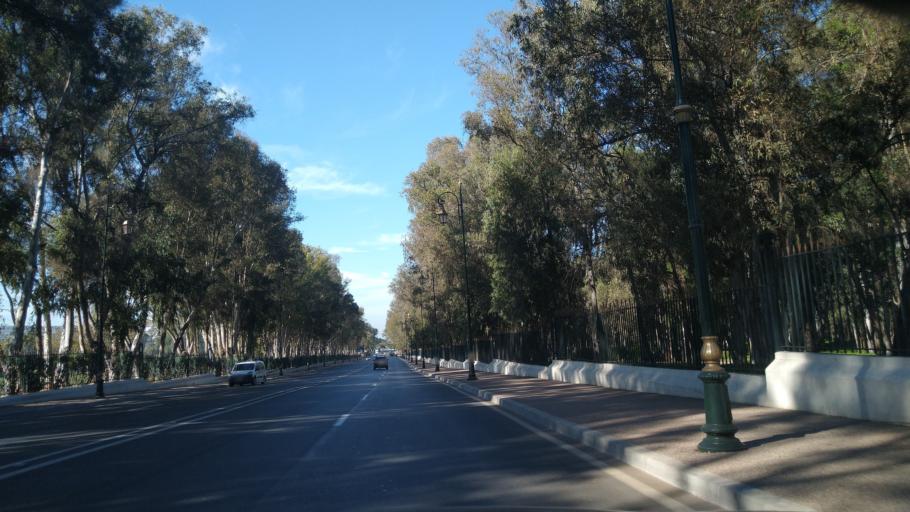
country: MA
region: Rabat-Sale-Zemmour-Zaer
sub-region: Rabat
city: Rabat
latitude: 33.9823
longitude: -6.8456
